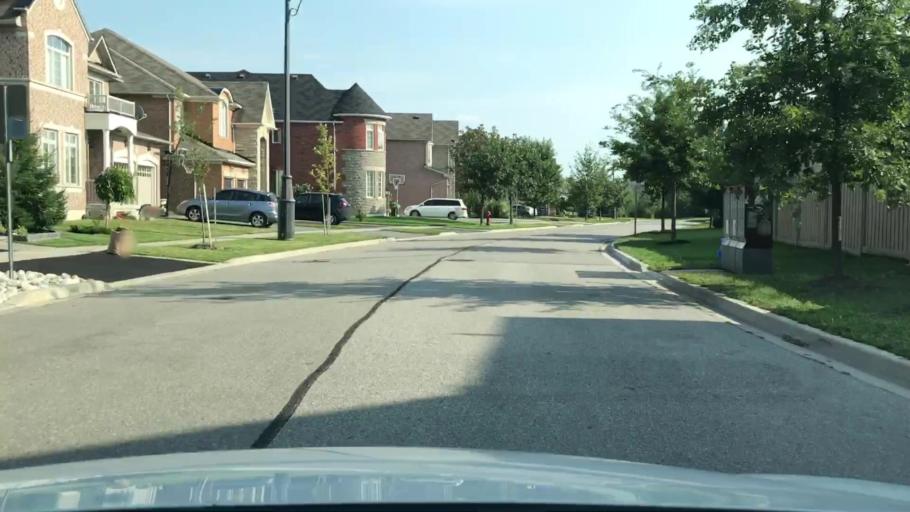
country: CA
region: Ontario
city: Newmarket
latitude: 44.0144
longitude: -79.4337
